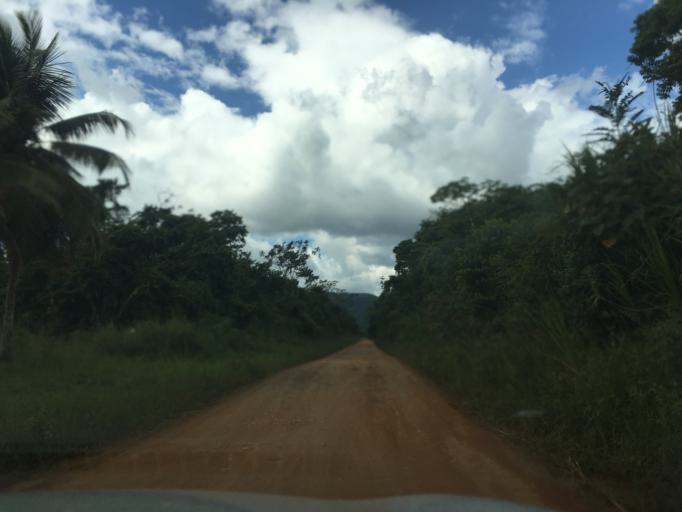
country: BZ
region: Stann Creek
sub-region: Dangriga
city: Dangriga
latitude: 16.9370
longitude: -88.3606
